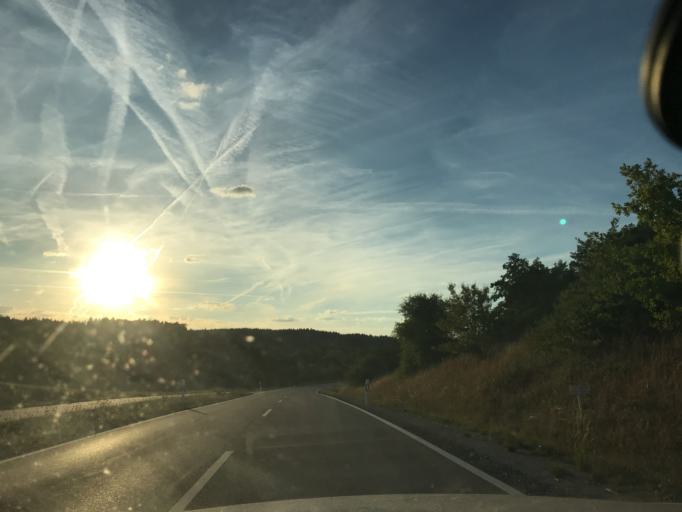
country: DE
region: Bavaria
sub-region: Upper Franconia
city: Pegnitz
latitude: 49.7216
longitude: 11.5678
